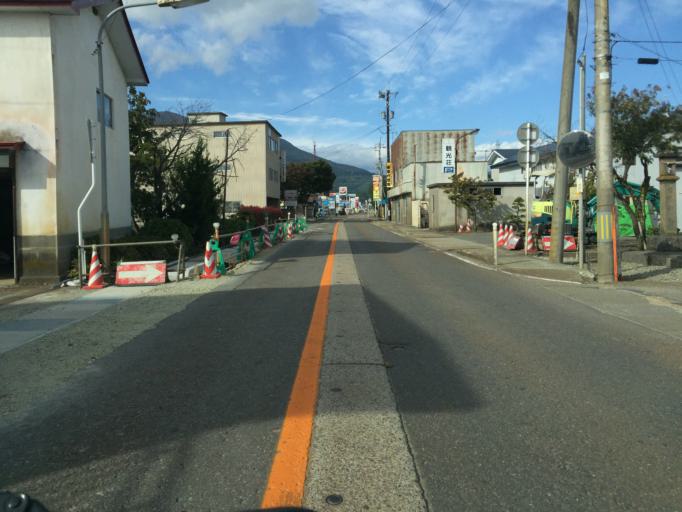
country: JP
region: Fukushima
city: Inawashiro
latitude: 37.5483
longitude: 140.1059
